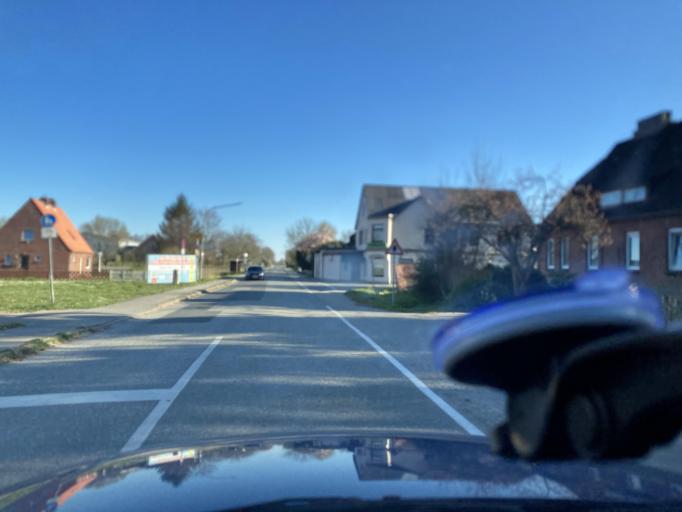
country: DE
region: Schleswig-Holstein
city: Norderwohrden
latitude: 54.2197
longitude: 9.0216
